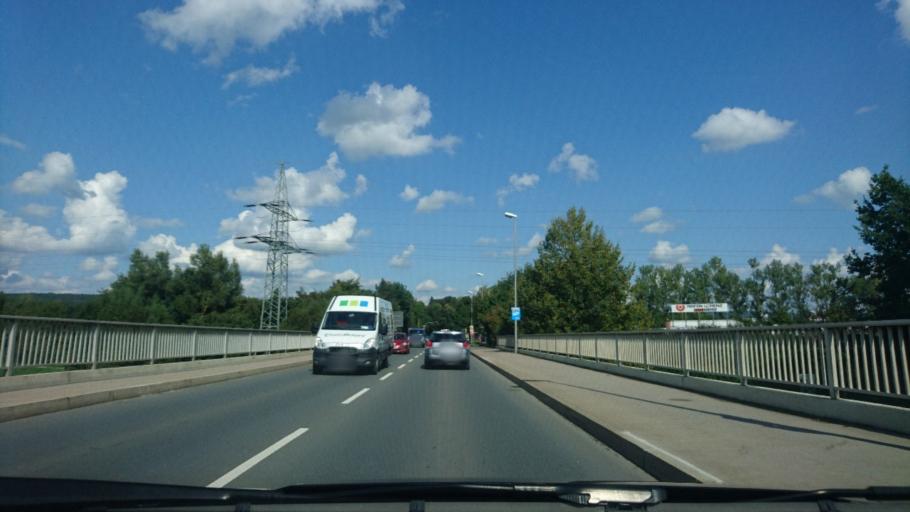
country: DE
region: Bavaria
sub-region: Upper Franconia
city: Bayreuth
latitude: 49.9515
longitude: 11.5629
